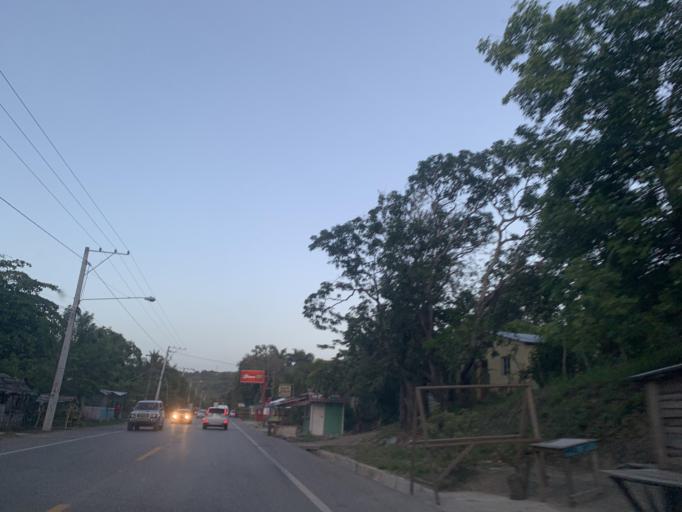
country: DO
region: Puerto Plata
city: Imbert
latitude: 19.7979
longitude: -70.7876
